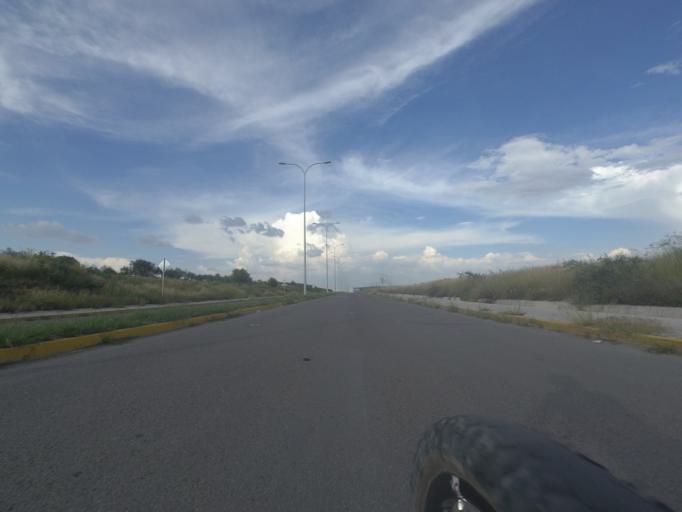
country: MX
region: Aguascalientes
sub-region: Aguascalientes
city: Penuelas (El Cienegal)
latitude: 21.7273
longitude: -102.2874
